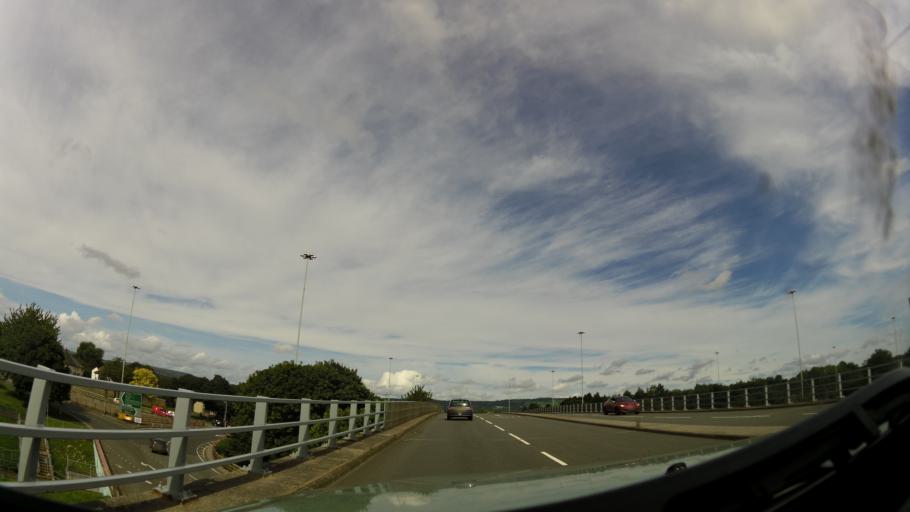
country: GB
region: Wales
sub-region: Cardiff
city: Cardiff
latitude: 51.5039
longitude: -3.1981
